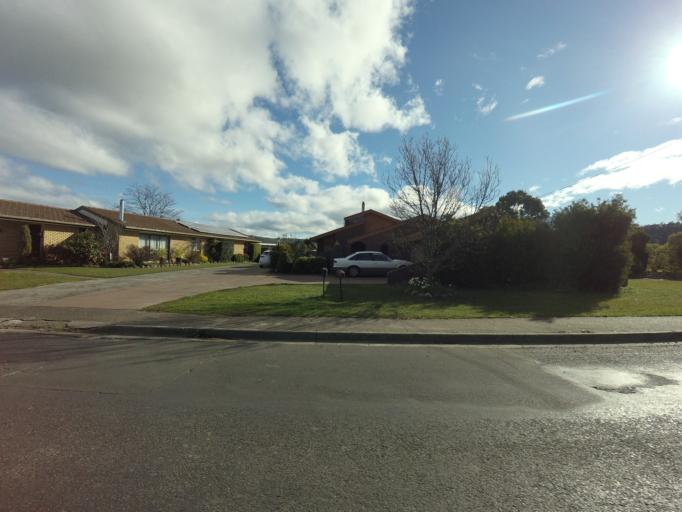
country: AU
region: Tasmania
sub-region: Derwent Valley
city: New Norfolk
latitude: -42.7672
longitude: 147.0457
